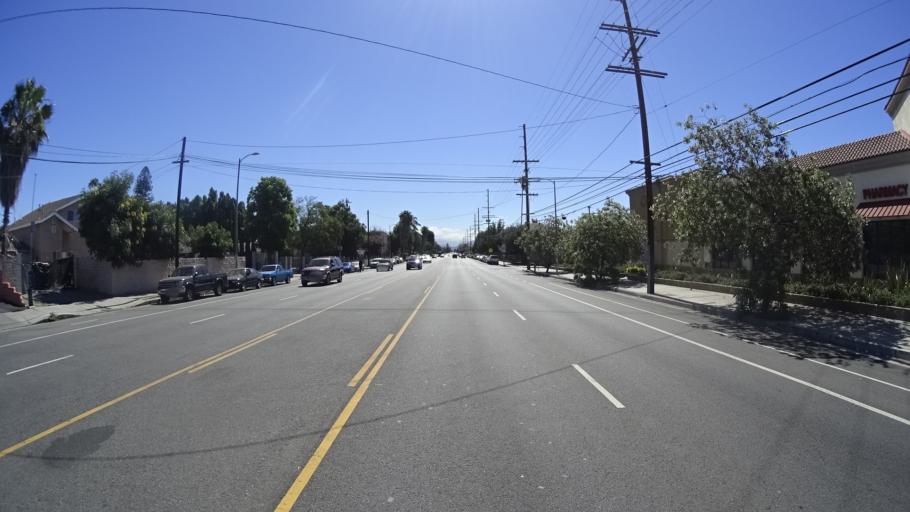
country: US
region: California
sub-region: Los Angeles County
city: Van Nuys
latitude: 34.2355
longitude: -118.4663
